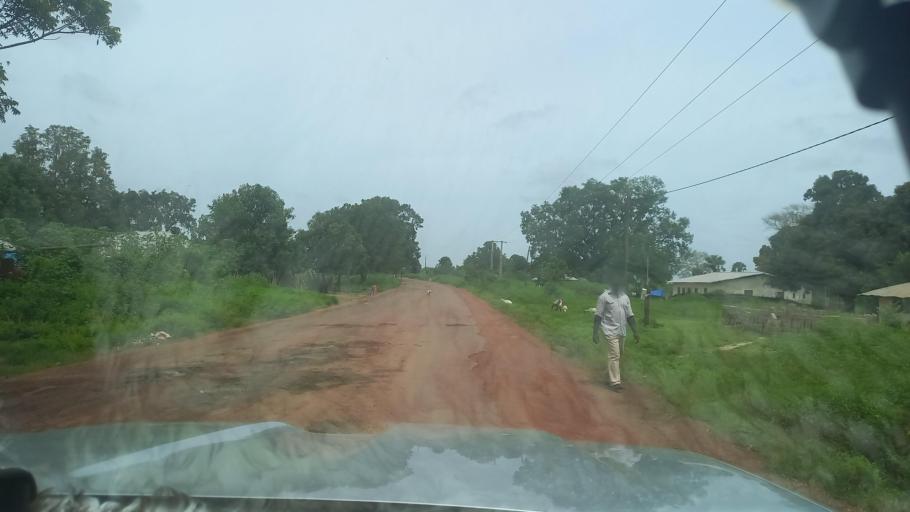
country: SN
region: Kolda
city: Marsassoum
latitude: 12.9153
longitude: -16.0097
